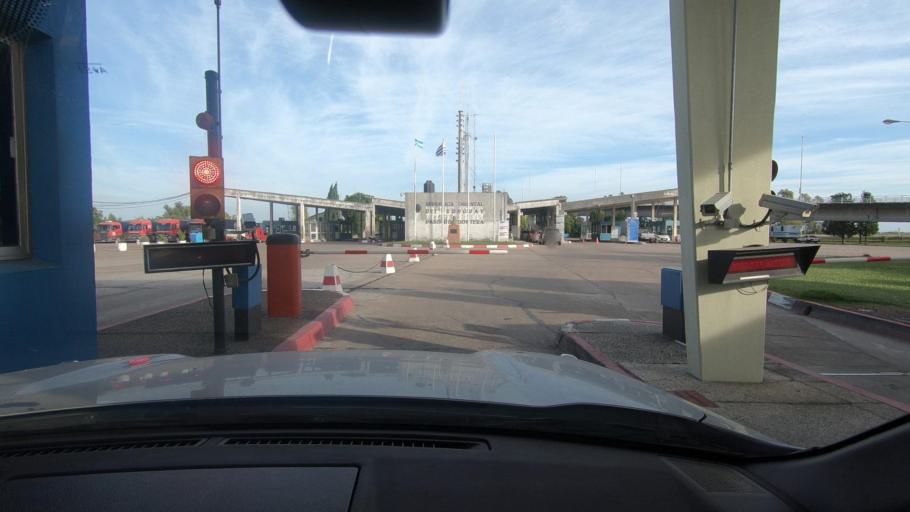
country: AR
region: Entre Rios
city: Colon
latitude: -32.2514
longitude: -58.1427
